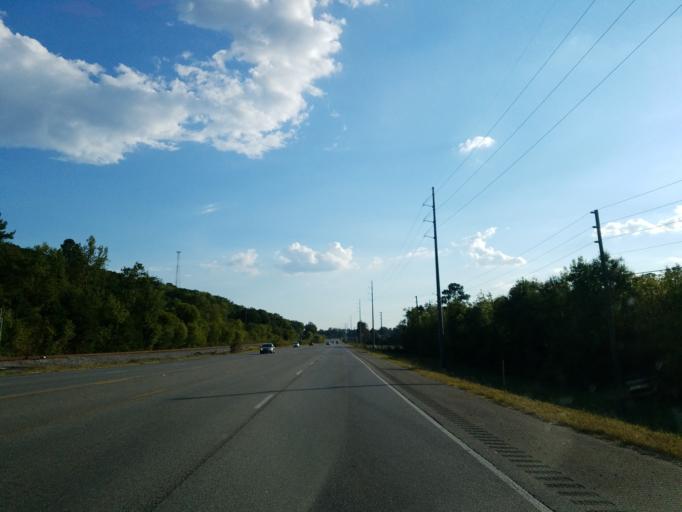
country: US
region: Georgia
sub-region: Murray County
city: Chatsworth
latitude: 34.8100
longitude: -84.7669
